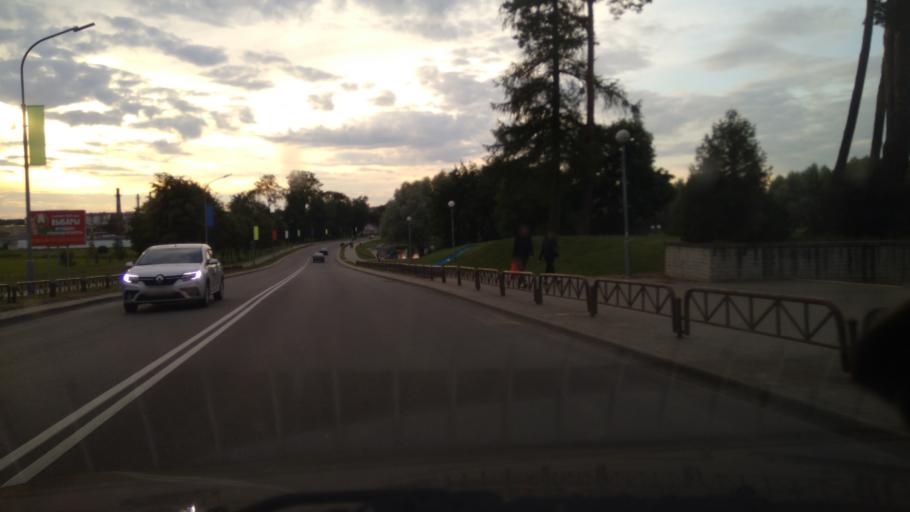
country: BY
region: Grodnenskaya
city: Shchuchin
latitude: 53.6066
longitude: 24.7416
